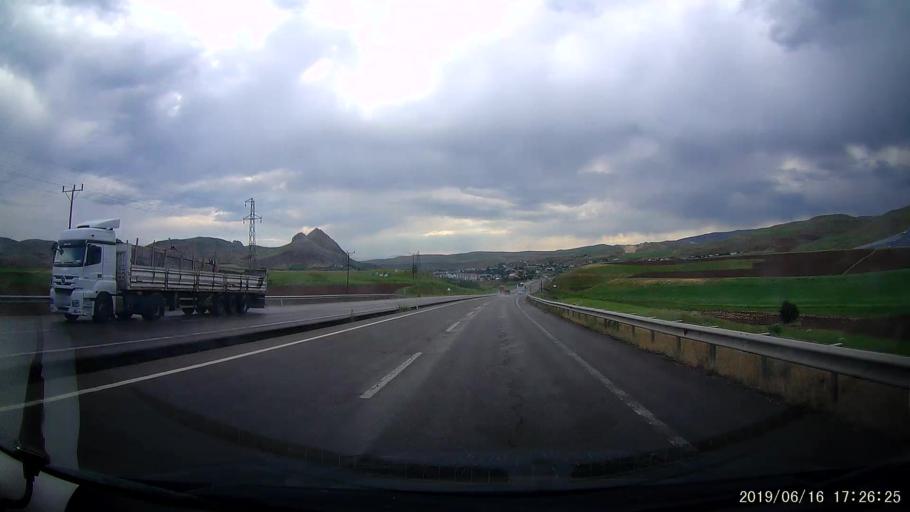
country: TR
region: Erzincan
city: Tercan
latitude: 39.7675
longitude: 40.4129
